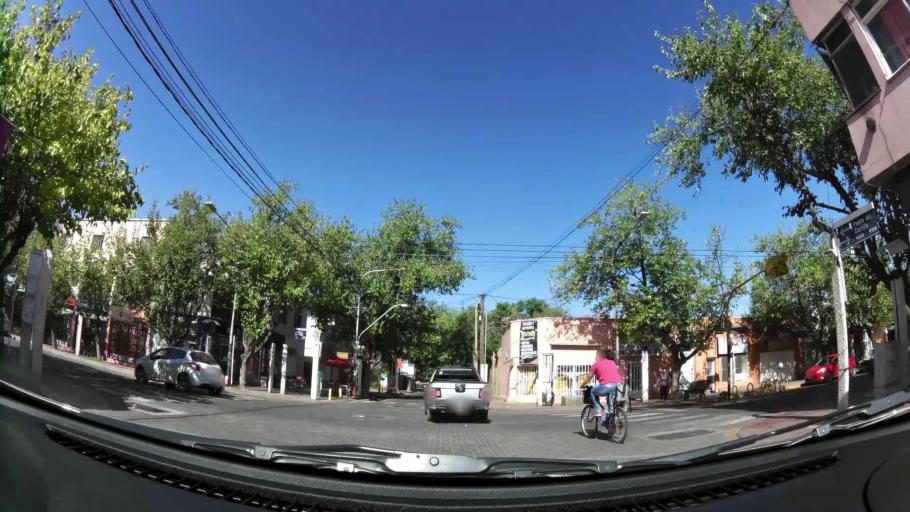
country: AR
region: Mendoza
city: Villa Nueva
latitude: -32.8987
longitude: -68.7872
